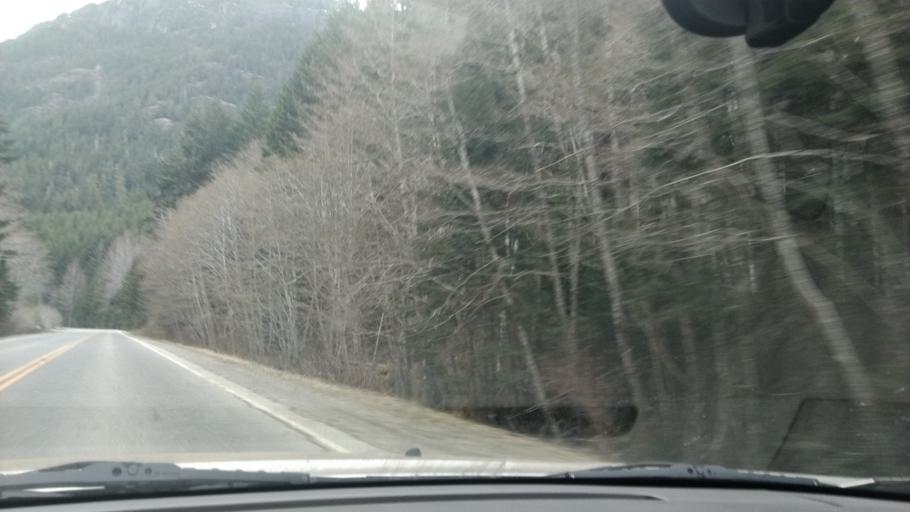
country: CA
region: British Columbia
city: Campbell River
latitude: 49.8540
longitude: -125.8338
